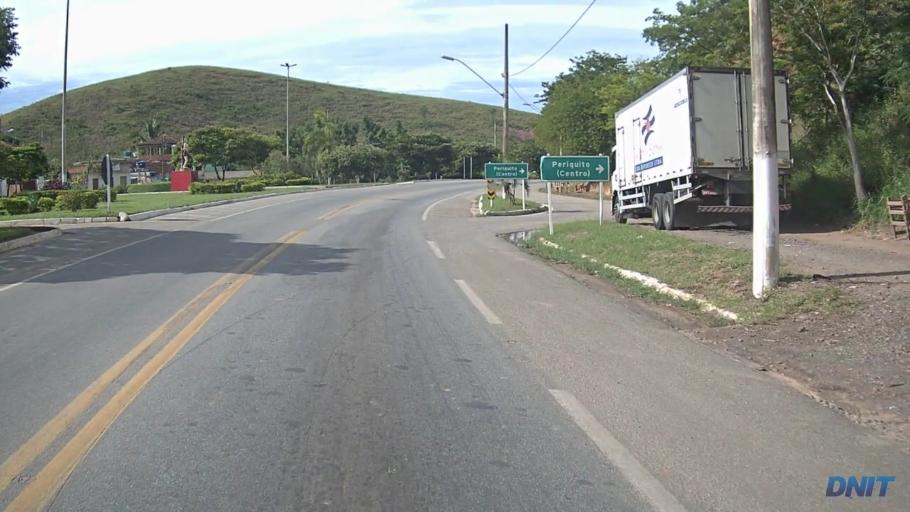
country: BR
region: Minas Gerais
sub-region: Belo Oriente
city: Belo Oriente
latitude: -19.1575
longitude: -42.2377
